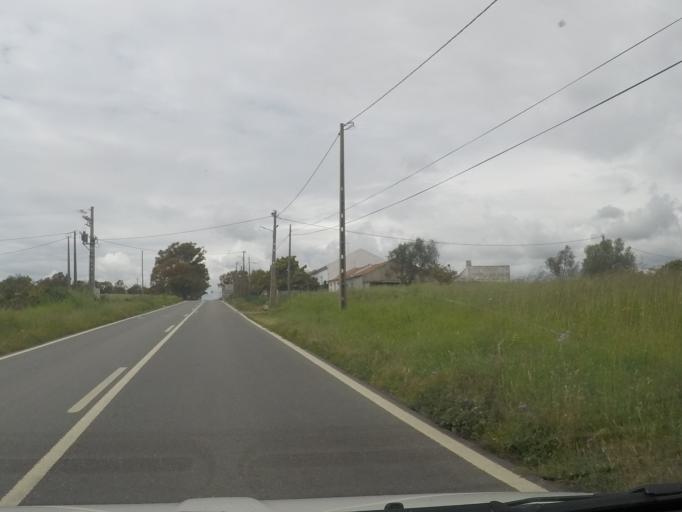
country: PT
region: Setubal
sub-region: Santiago do Cacem
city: Cercal
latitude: 37.8623
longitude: -8.7177
